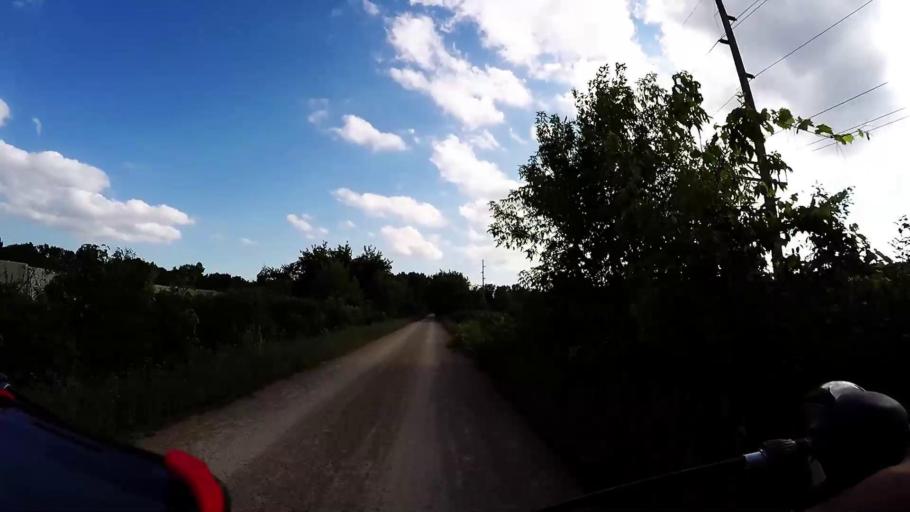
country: US
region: Minnesota
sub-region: Hennepin County
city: Eden Prairie
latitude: 44.8876
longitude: -93.4579
